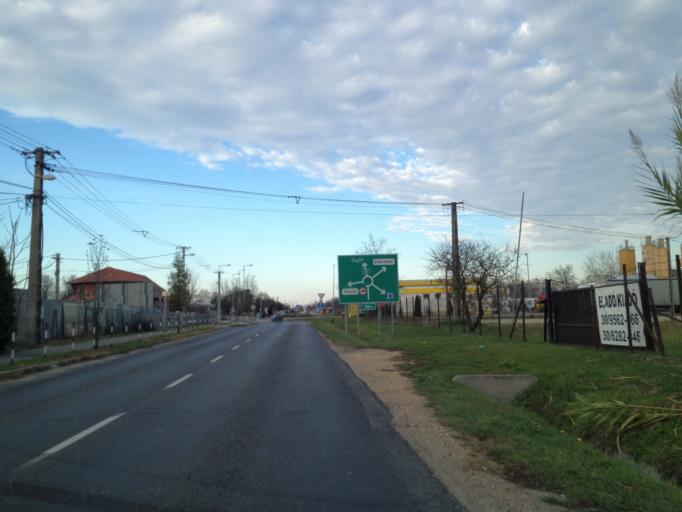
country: HU
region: Gyor-Moson-Sopron
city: Nyul
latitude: 47.5940
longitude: 17.6873
